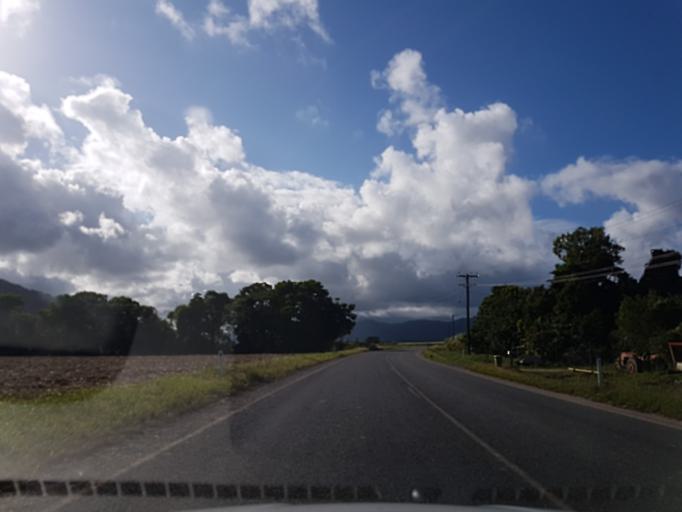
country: AU
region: Queensland
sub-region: Cairns
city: Port Douglas
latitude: -16.3029
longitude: 145.3895
